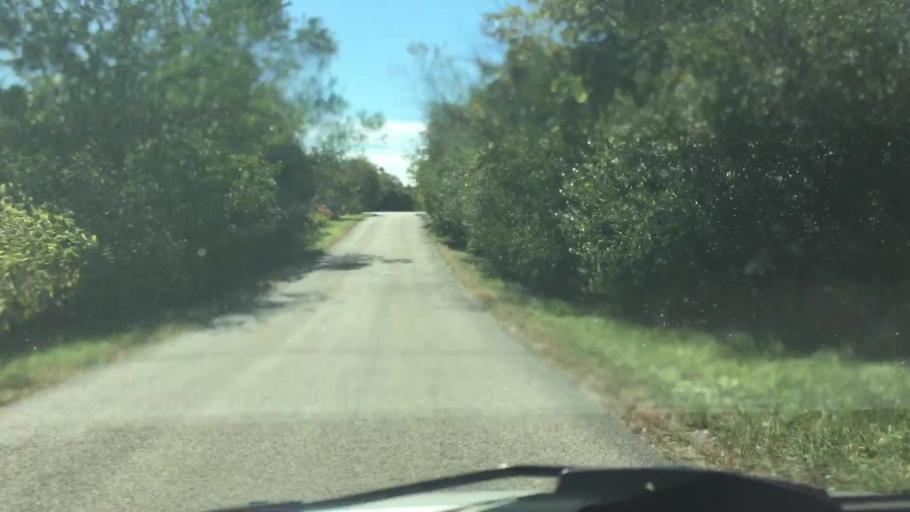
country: US
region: Wisconsin
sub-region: Waukesha County
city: North Prairie
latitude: 42.9318
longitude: -88.4346
